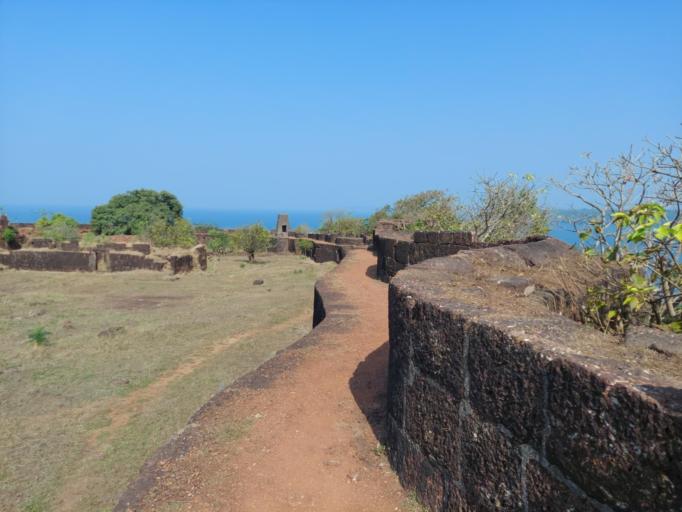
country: IN
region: Maharashtra
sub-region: Ratnagiri
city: Guhagar
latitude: 17.3008
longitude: 73.2220
